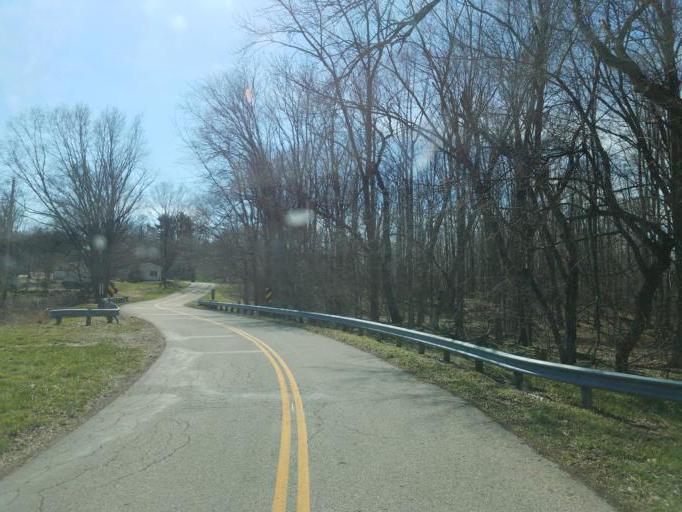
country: US
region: Ohio
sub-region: Richland County
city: Lincoln Heights
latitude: 40.8008
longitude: -82.4234
